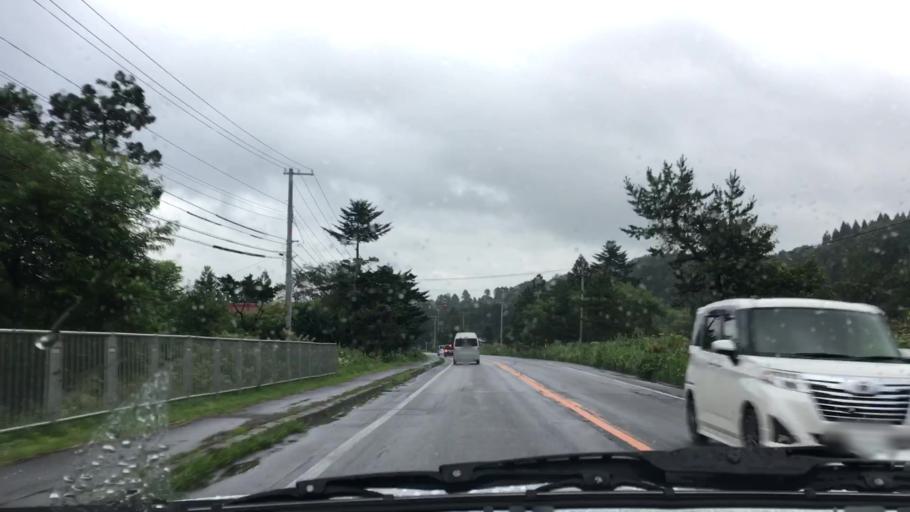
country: JP
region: Hokkaido
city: Nanae
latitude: 42.2248
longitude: 140.3445
